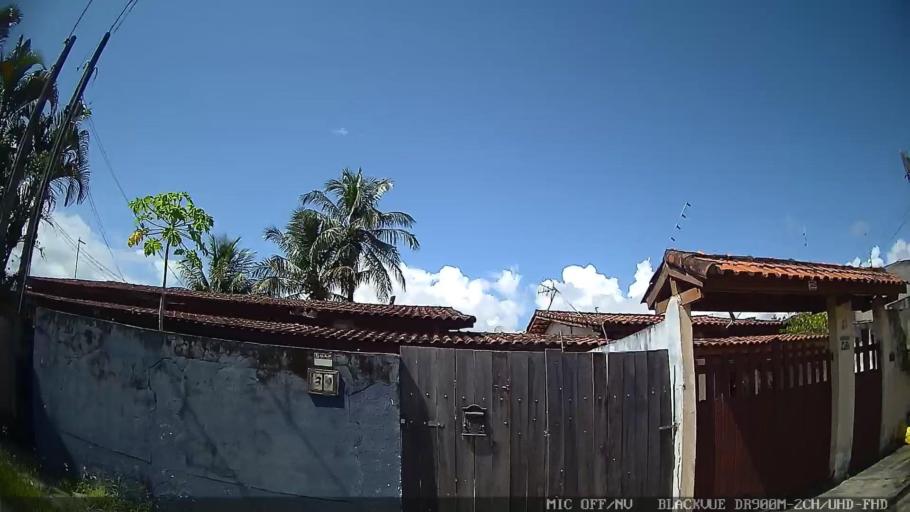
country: BR
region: Sao Paulo
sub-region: Caraguatatuba
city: Caraguatatuba
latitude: -23.6814
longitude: -45.4381
